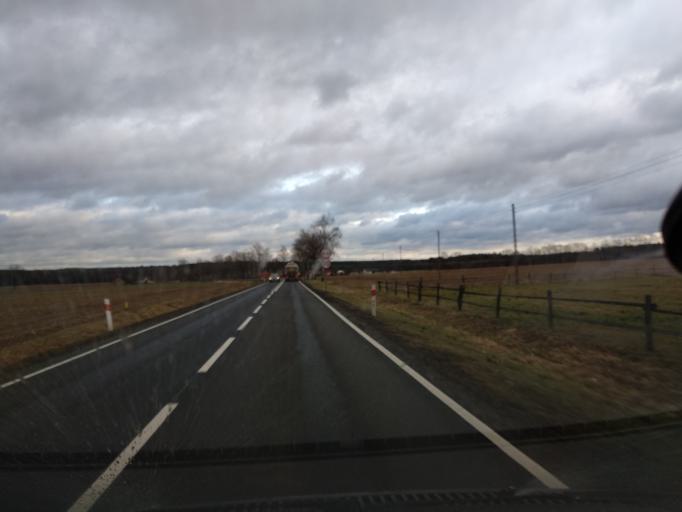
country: PL
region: Lower Silesian Voivodeship
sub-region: Powiat olesnicki
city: Miedzyborz
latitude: 51.3443
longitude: 17.5939
